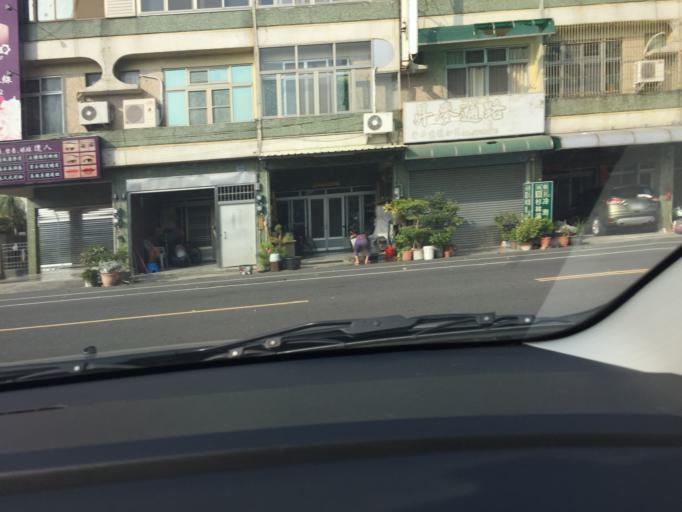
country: TW
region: Taiwan
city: Xinying
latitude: 23.1930
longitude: 120.3131
